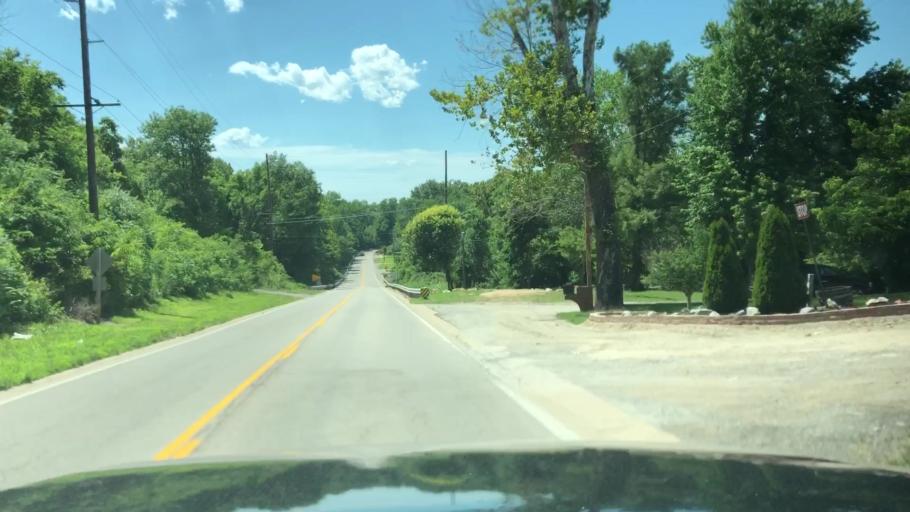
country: US
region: Illinois
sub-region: Saint Clair County
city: Centreville
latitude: 38.5537
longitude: -90.0897
